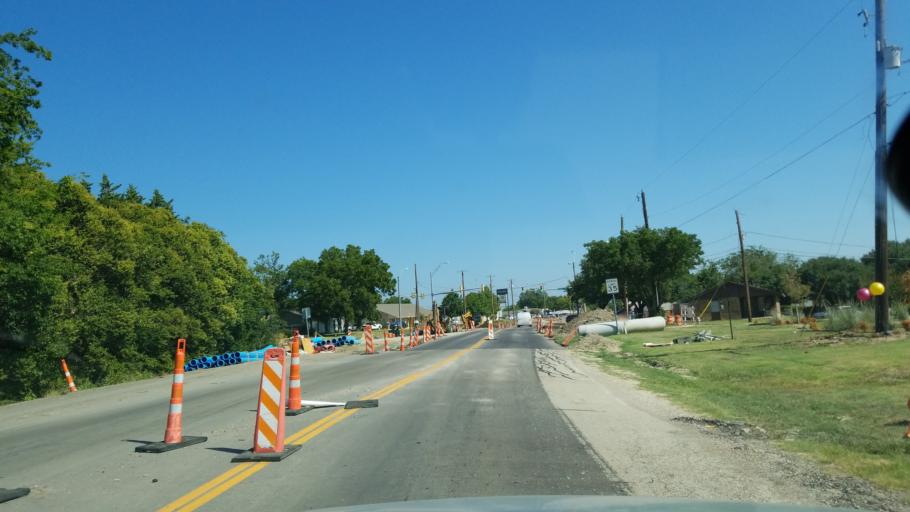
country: US
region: Texas
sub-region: Tarrant County
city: Mansfield
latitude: 32.5582
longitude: -97.1420
